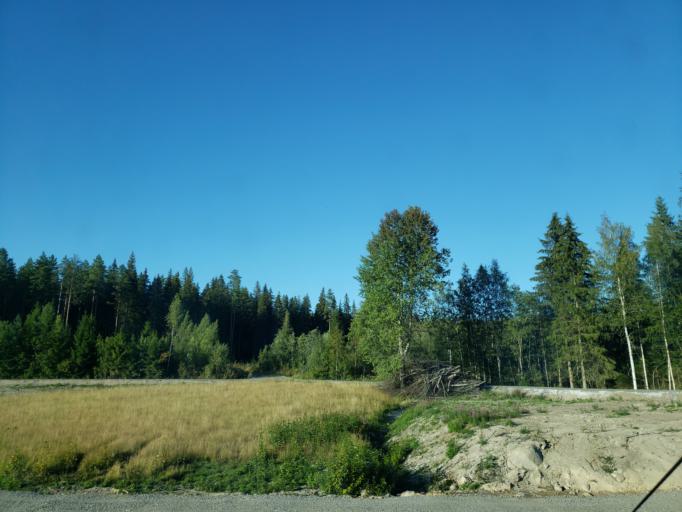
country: FI
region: South Karelia
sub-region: Lappeenranta
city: Nuijamaa
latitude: 60.8573
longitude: 28.3313
